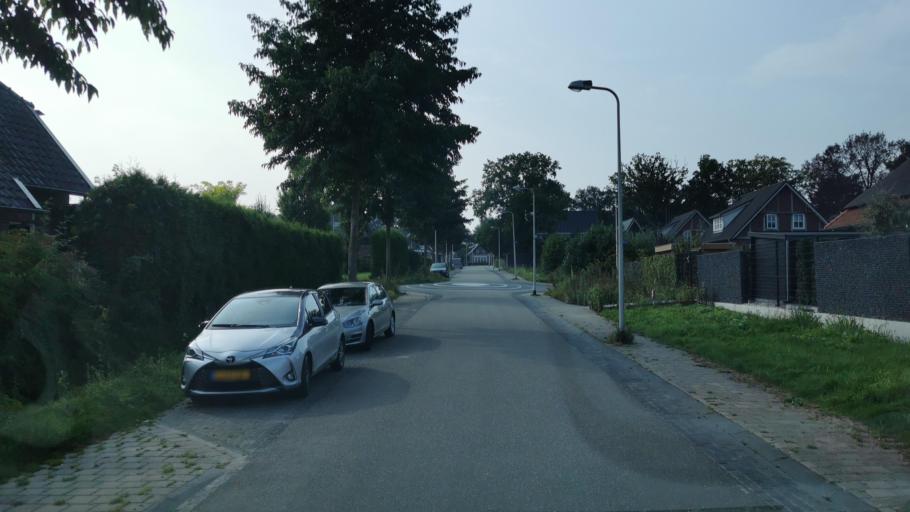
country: NL
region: Overijssel
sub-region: Gemeente Losser
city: Losser
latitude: 52.3114
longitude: 6.9994
